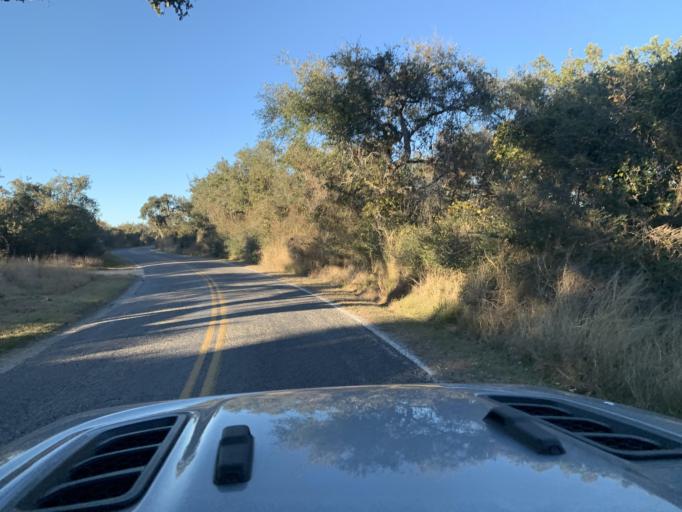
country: US
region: Texas
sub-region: Aransas County
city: Fulton
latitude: 28.1488
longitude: -96.9842
